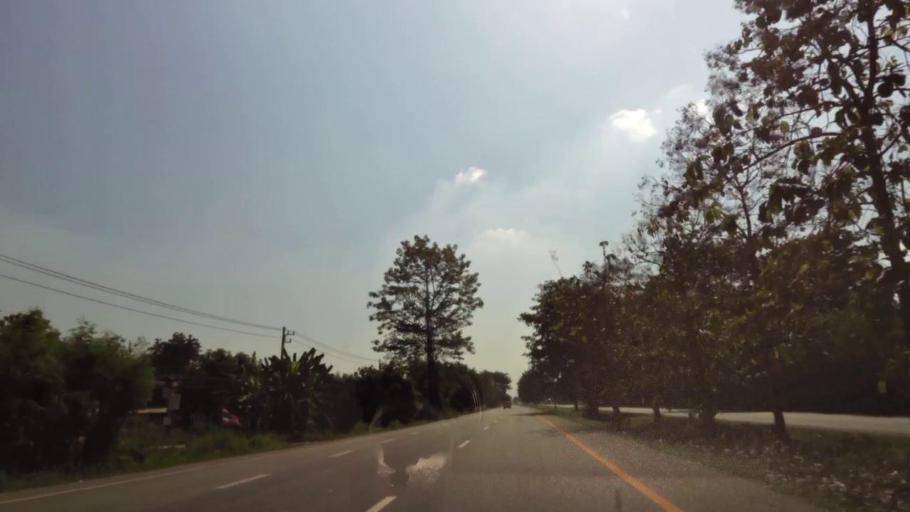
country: TH
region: Phichit
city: Bueng Na Rang
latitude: 16.2321
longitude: 100.1257
